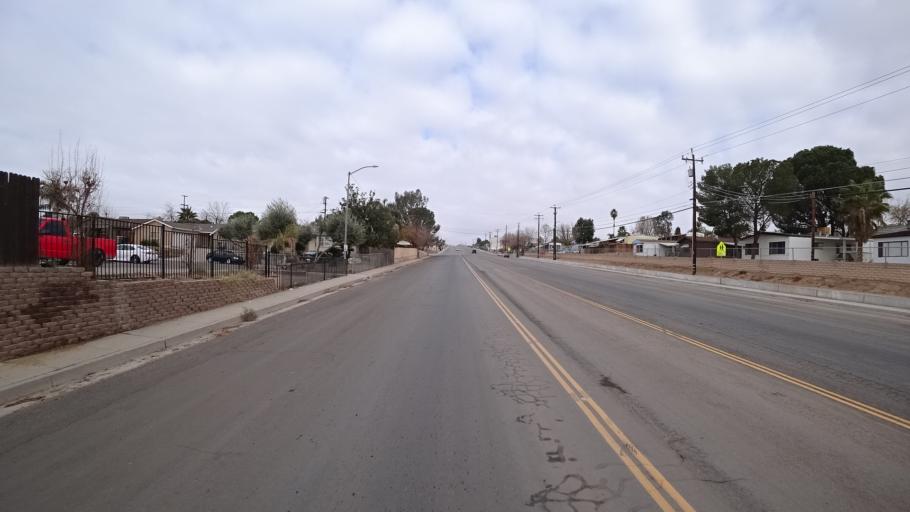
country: US
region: California
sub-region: Kern County
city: Bakersfield
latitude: 35.3787
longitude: -118.9143
